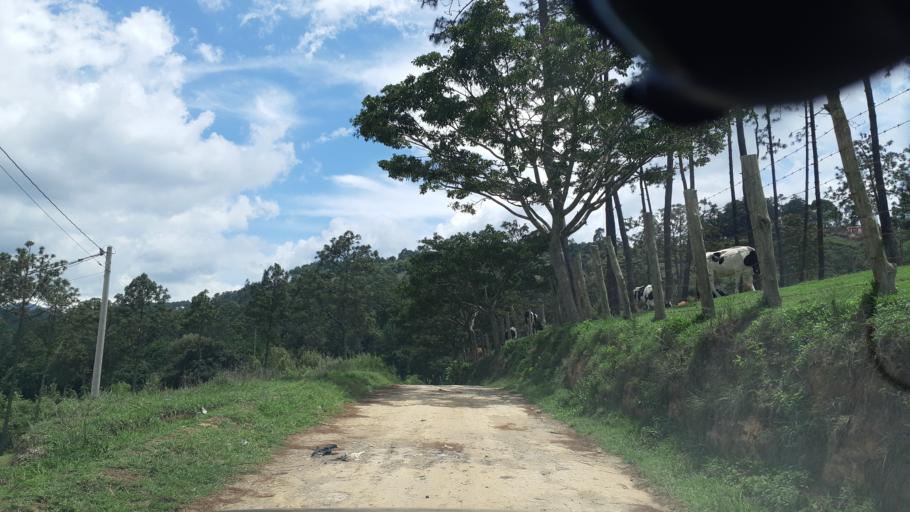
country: GT
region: Chimaltenango
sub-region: Municipio de Chimaltenango
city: Chimaltenango
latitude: 14.6604
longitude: -90.8463
